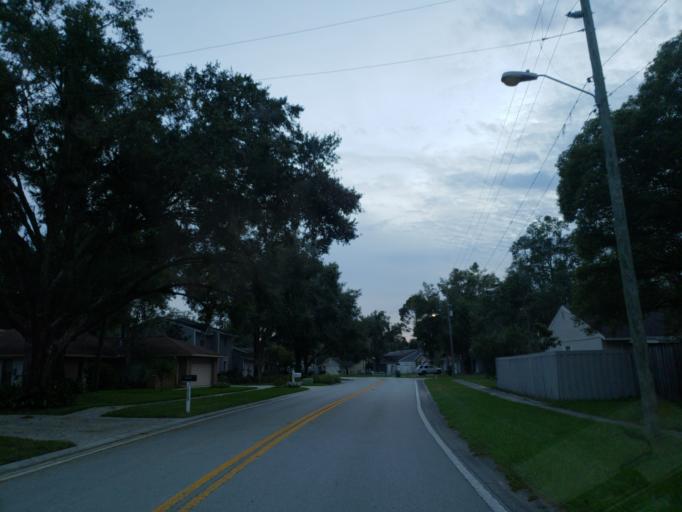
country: US
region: Florida
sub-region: Hillsborough County
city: Lutz
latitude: 28.1814
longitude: -82.4591
